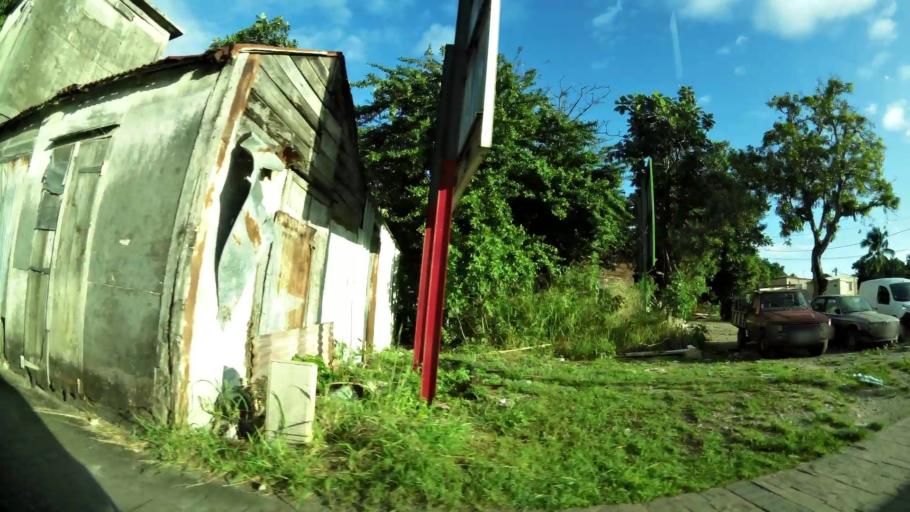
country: GP
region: Guadeloupe
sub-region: Guadeloupe
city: Pointe-a-Pitre
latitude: 16.2277
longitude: -61.5311
